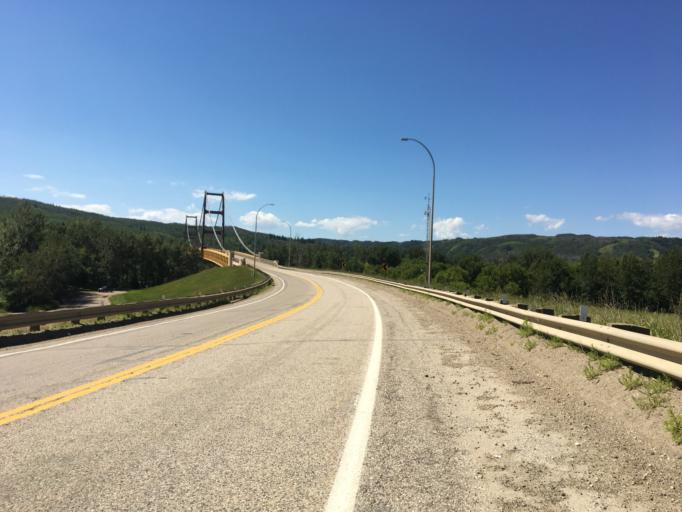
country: CA
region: Alberta
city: Fairview
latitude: 55.9242
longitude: -118.5995
